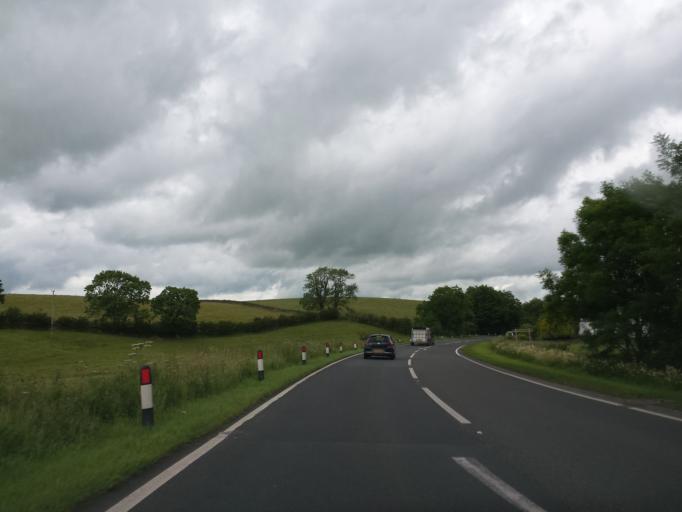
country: GB
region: Scotland
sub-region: Dumfries and Galloway
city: Castle Douglas
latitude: 55.0033
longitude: -3.8752
